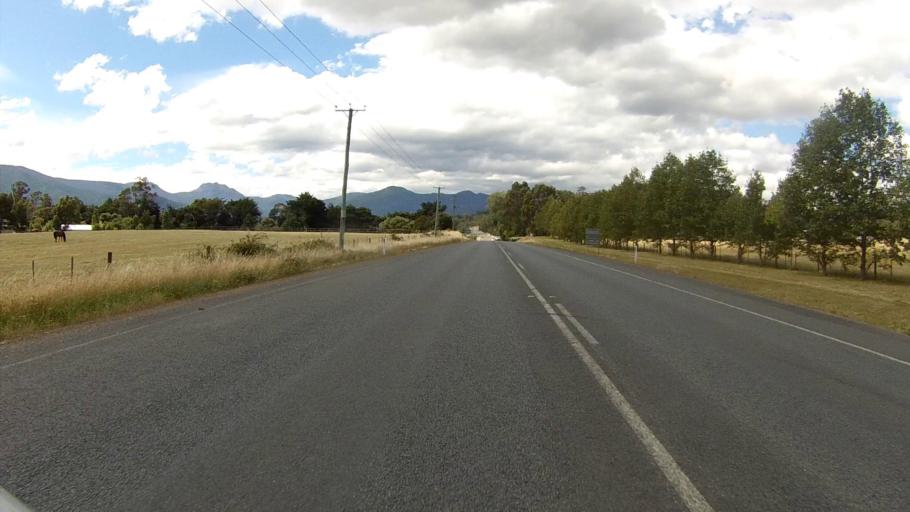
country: AU
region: Tasmania
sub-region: Huon Valley
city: Huonville
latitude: -42.9864
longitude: 147.0890
